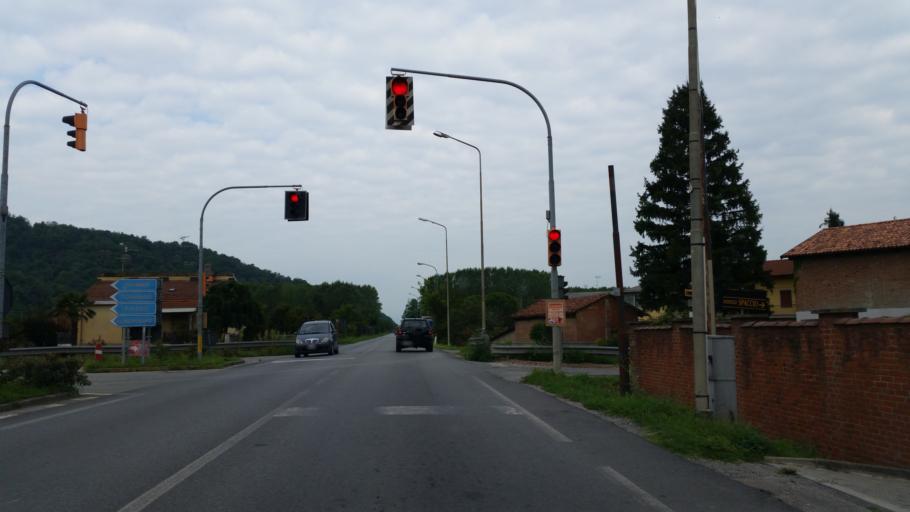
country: IT
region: Piedmont
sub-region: Provincia di Torino
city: Lauriano
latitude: 45.1638
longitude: 7.9966
